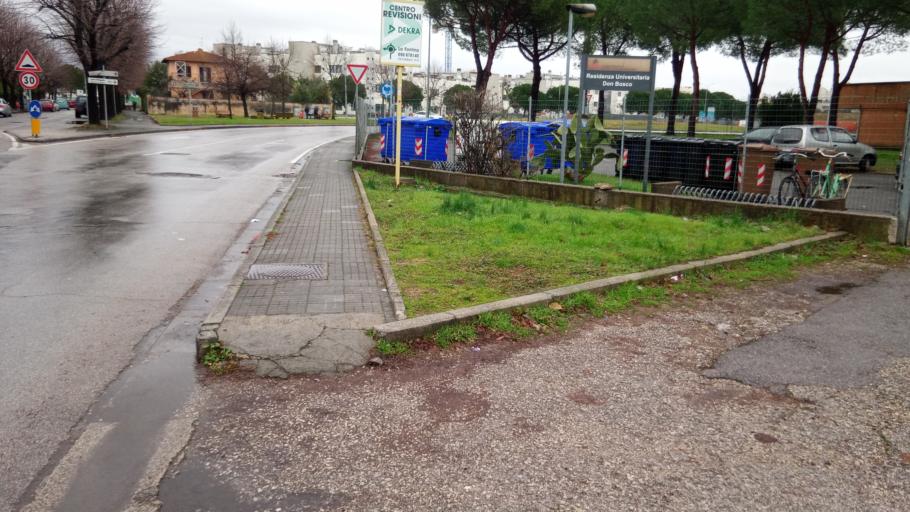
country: IT
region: Tuscany
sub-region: Province of Pisa
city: Pisa
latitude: 43.7194
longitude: 10.4182
